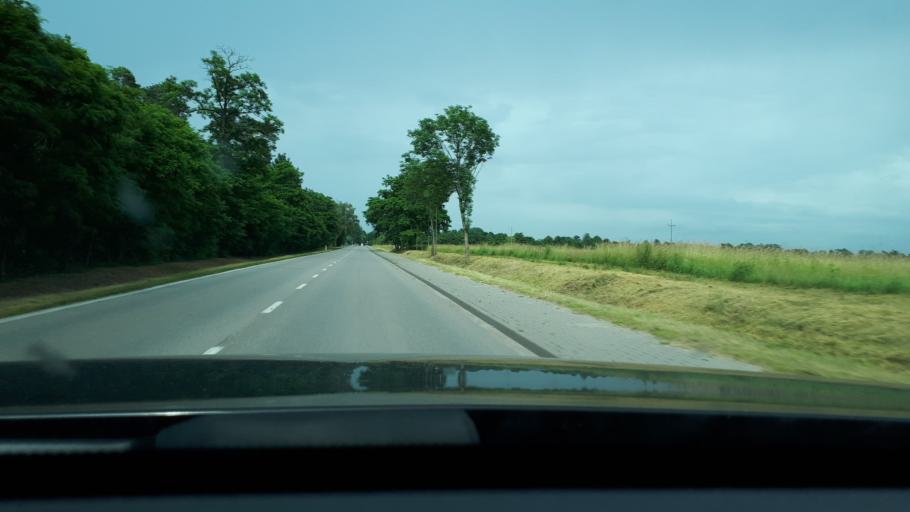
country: PL
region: Masovian Voivodeship
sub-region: Powiat warszawski zachodni
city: Leszno
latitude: 52.2623
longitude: 20.6358
